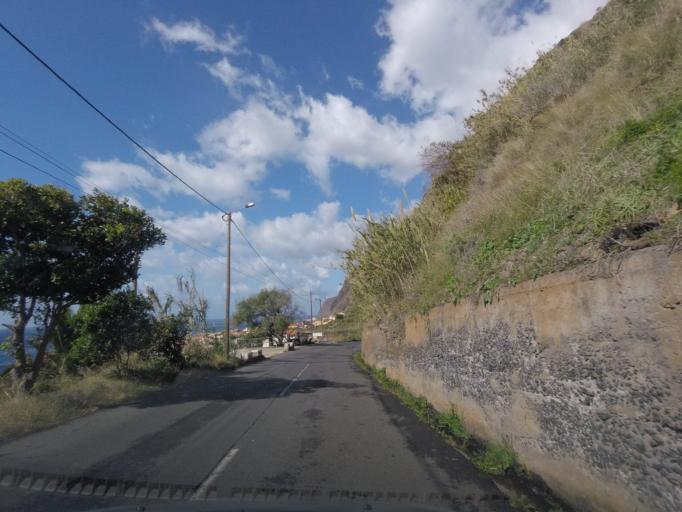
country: PT
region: Madeira
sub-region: Calheta
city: Estreito da Calheta
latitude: 32.7366
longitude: -17.2084
